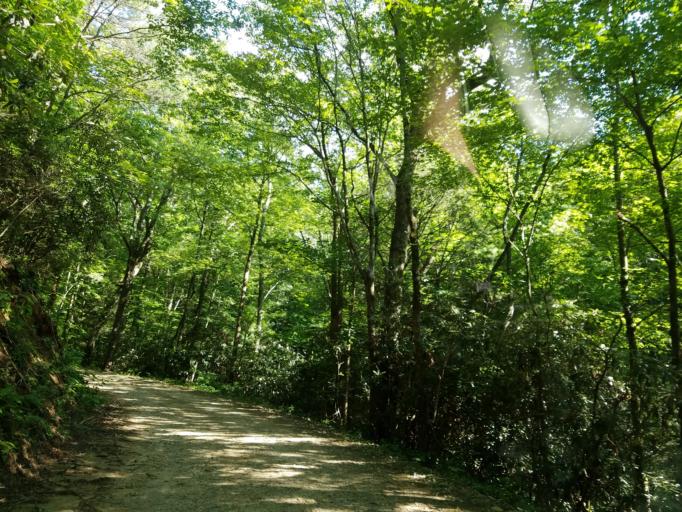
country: US
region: Georgia
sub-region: Dawson County
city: Dawsonville
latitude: 34.5865
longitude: -84.1996
